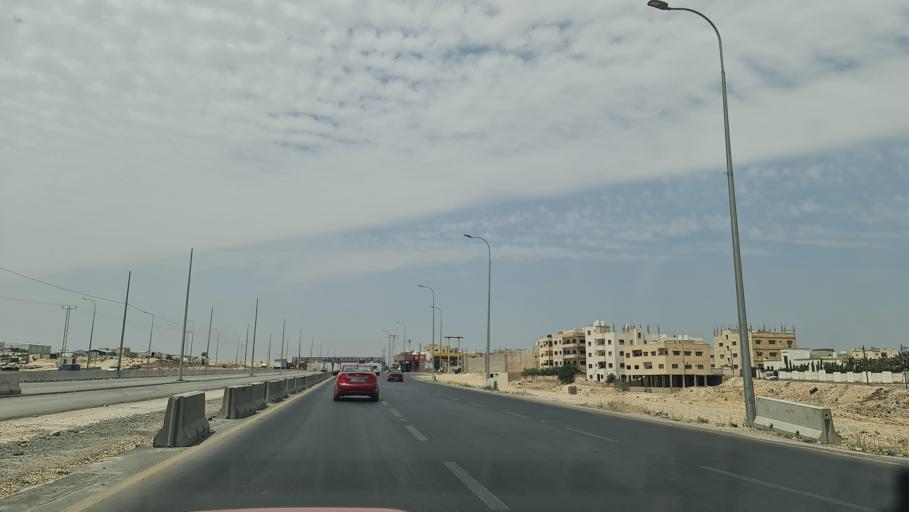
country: JO
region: Zarqa
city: Russeifa
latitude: 32.0159
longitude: 36.0678
